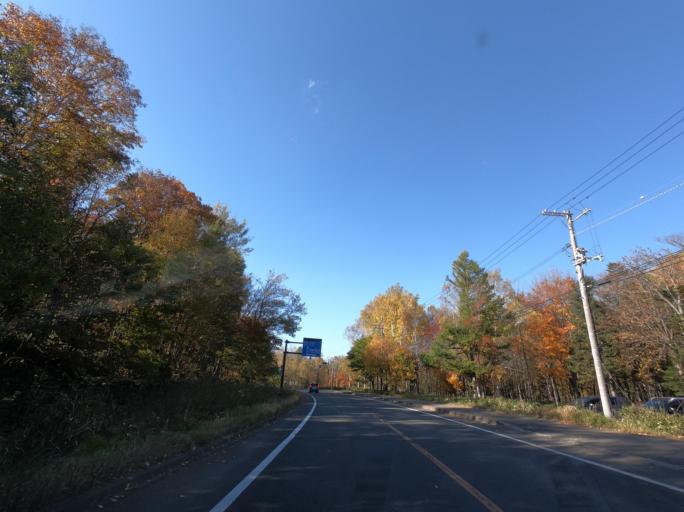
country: JP
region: Hokkaido
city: Bihoro
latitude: 43.4340
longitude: 144.0881
